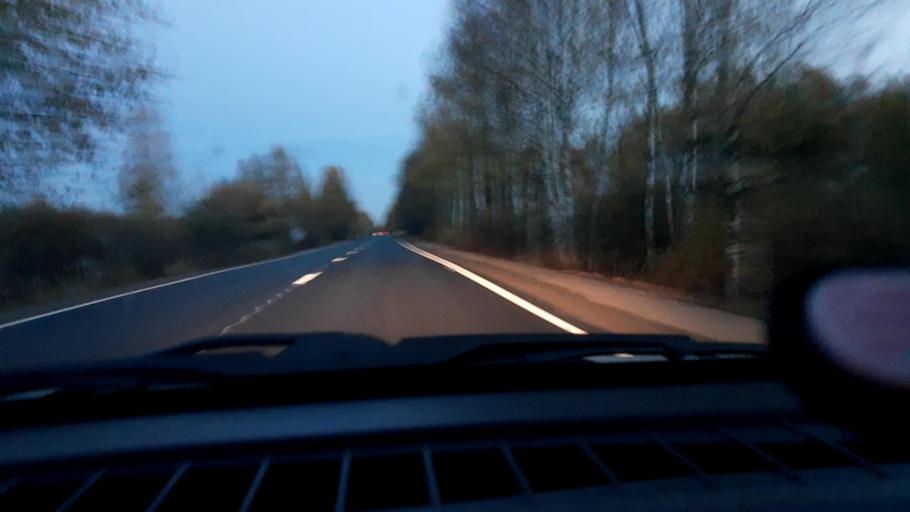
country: RU
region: Nizjnij Novgorod
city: Novaya Balakhna
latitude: 56.5632
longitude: 43.7247
